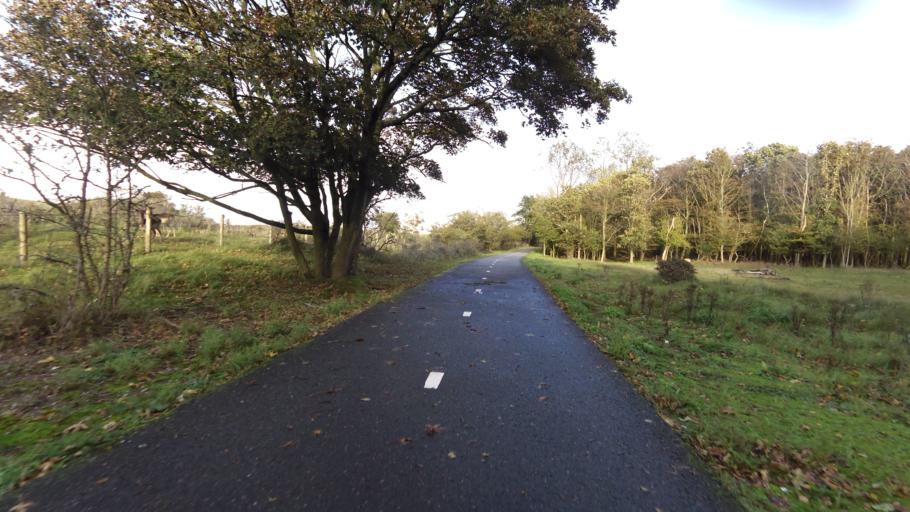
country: NL
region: South Holland
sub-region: Gemeente Noordwijkerhout
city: Noordwijkerhout
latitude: 52.2953
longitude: 4.4956
